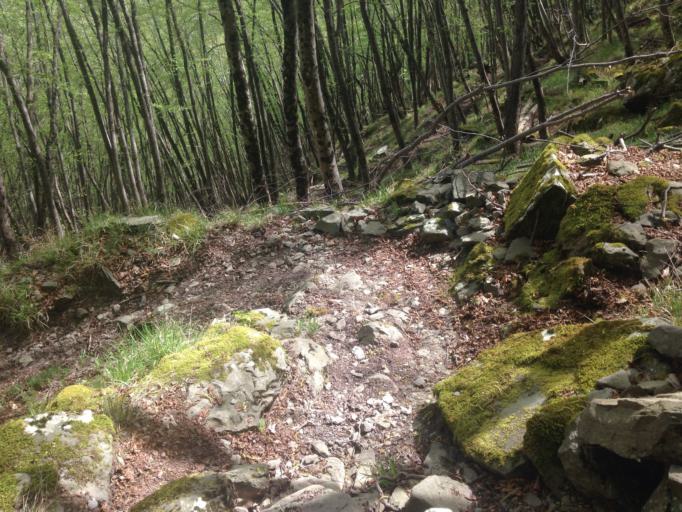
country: IT
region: Emilia-Romagna
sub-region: Provincia di Bologna
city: Lizzano in Belvedere
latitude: 44.1536
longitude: 10.8915
